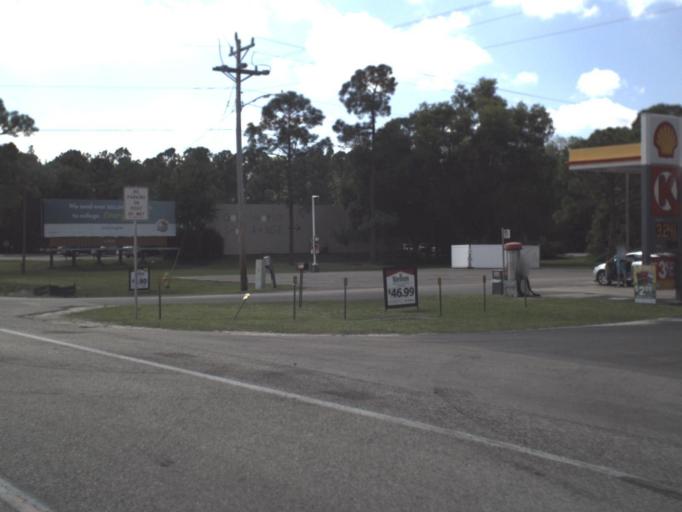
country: US
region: Florida
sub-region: Lee County
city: Suncoast Estates
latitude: 26.7420
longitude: -81.9160
